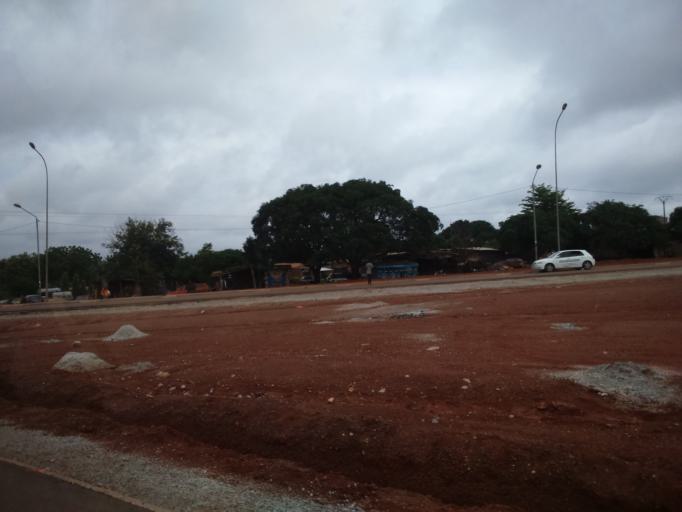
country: CI
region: Moyen-Comoe
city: Abengourou
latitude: 6.7231
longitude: -3.5098
